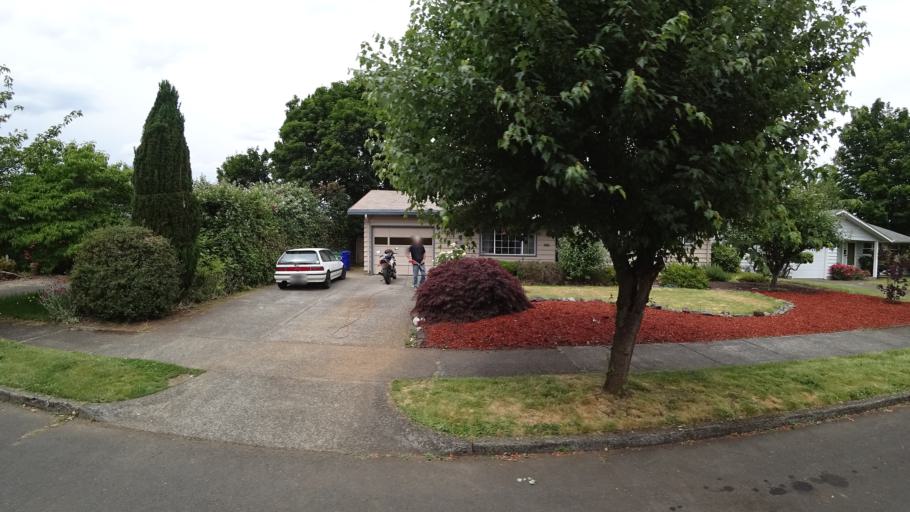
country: US
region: Oregon
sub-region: Multnomah County
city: Lents
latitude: 45.5088
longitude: -122.5627
